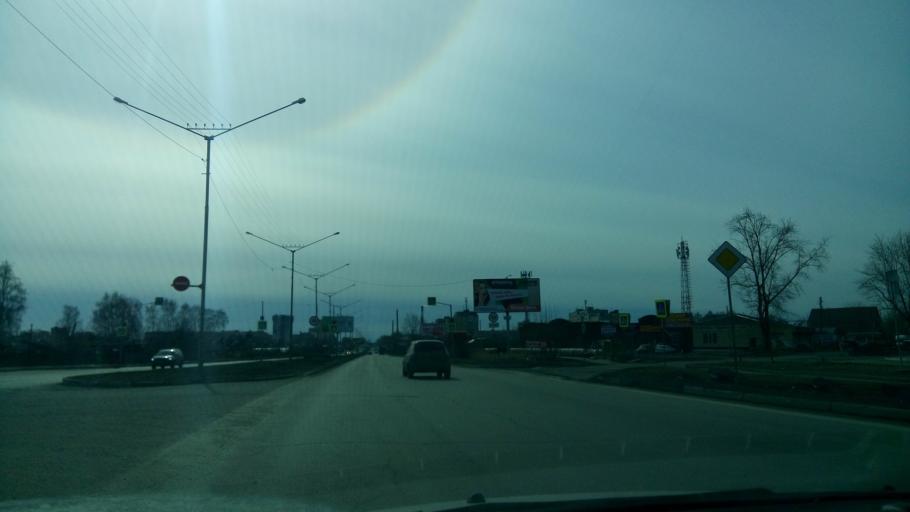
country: RU
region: Sverdlovsk
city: Nizhniy Tagil
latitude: 57.8942
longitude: 59.9409
